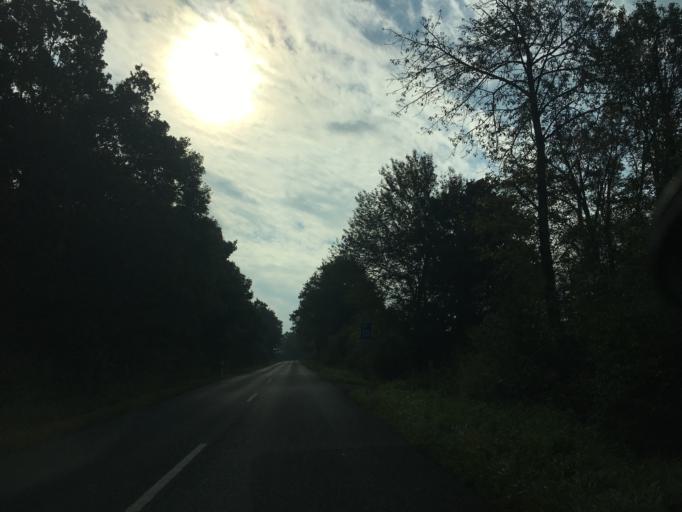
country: DE
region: Hesse
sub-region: Regierungsbezirk Darmstadt
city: Steinau an der Strasse
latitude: 50.3022
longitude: 9.4826
